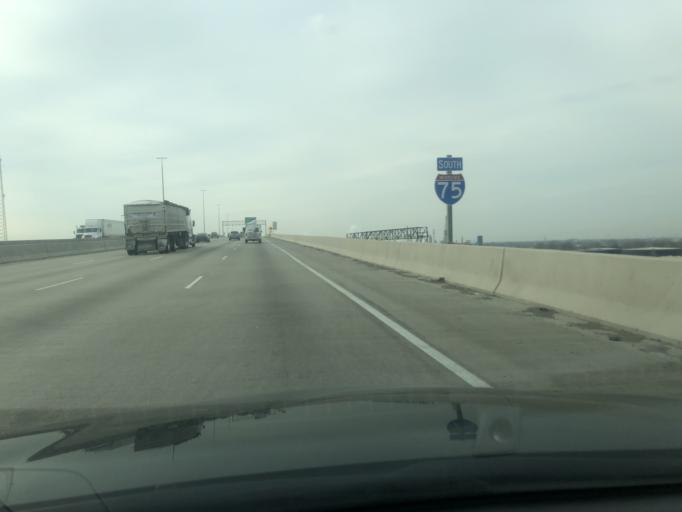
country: US
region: Michigan
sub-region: Wayne County
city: River Rouge
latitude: 42.2886
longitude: -83.1366
